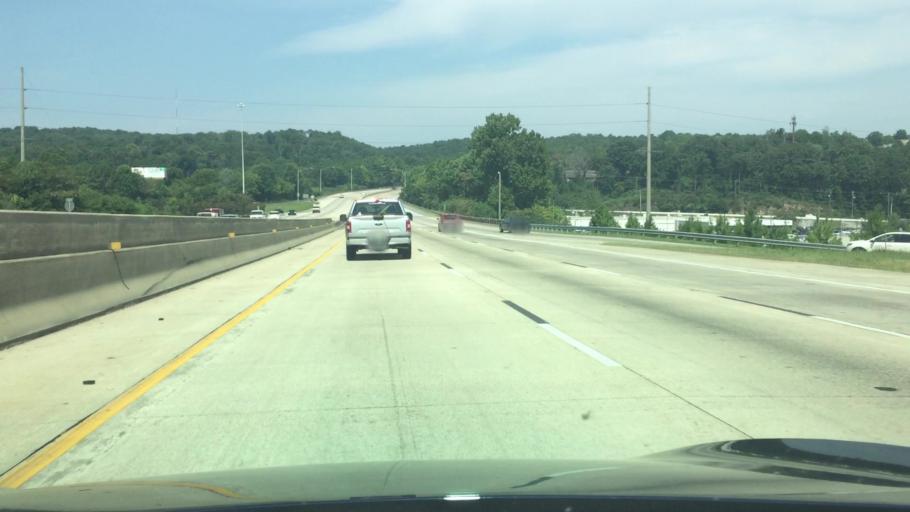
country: US
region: Alabama
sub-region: Jefferson County
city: Hoover
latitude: 33.4116
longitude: -86.8047
